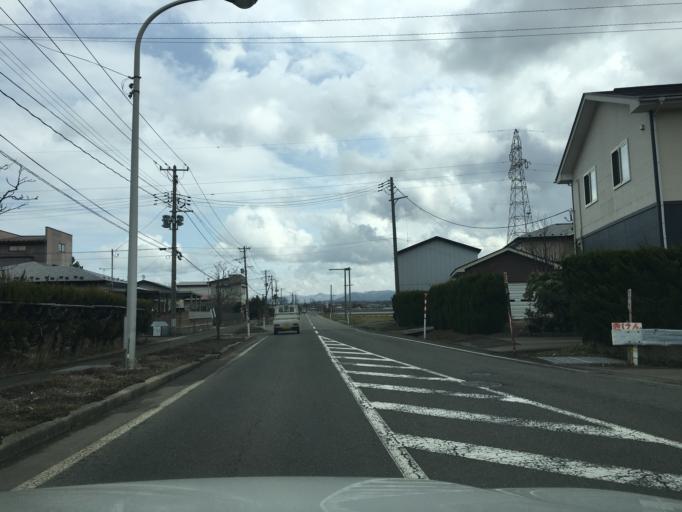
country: JP
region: Akita
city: Tenno
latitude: 39.9362
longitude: 140.0848
